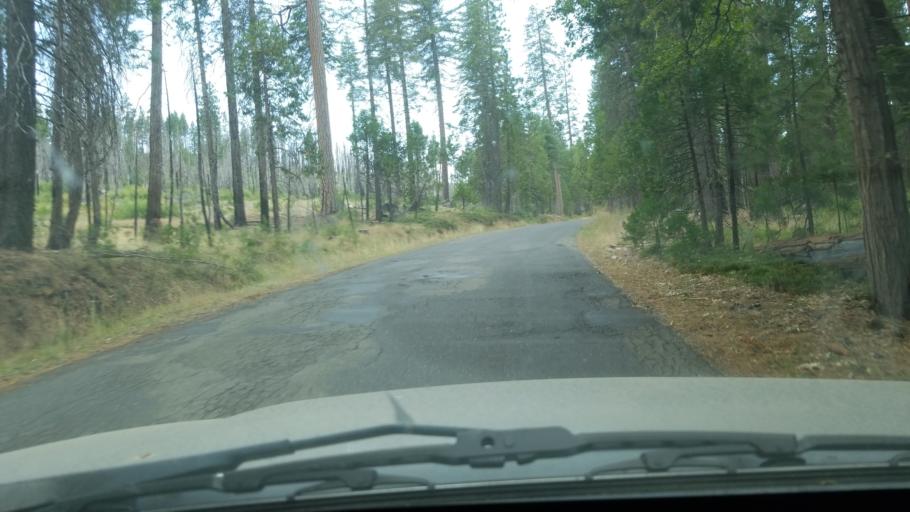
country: US
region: California
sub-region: Mariposa County
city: Midpines
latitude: 37.8274
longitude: -119.8574
